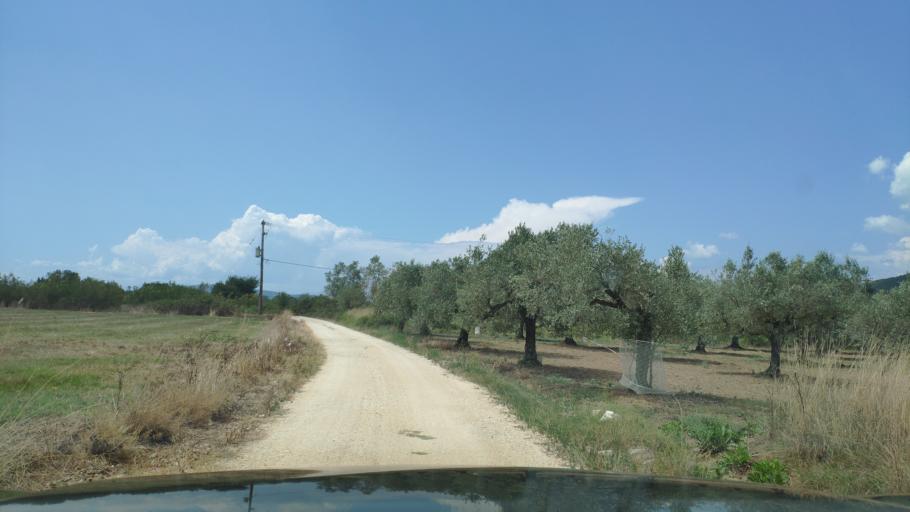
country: GR
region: West Greece
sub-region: Nomos Aitolias kai Akarnanias
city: Menidi
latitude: 39.0541
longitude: 21.0974
